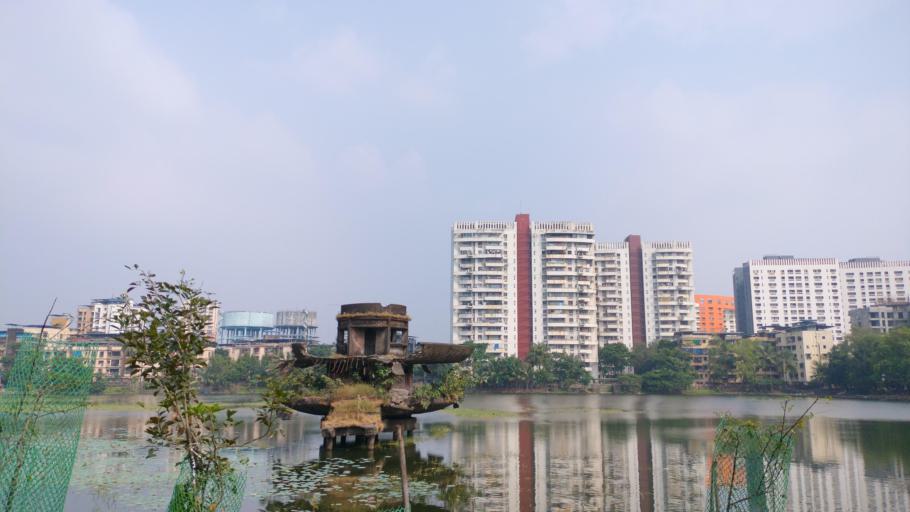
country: IN
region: Maharashtra
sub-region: Thane
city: Thane
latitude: 19.1894
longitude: 72.9560
